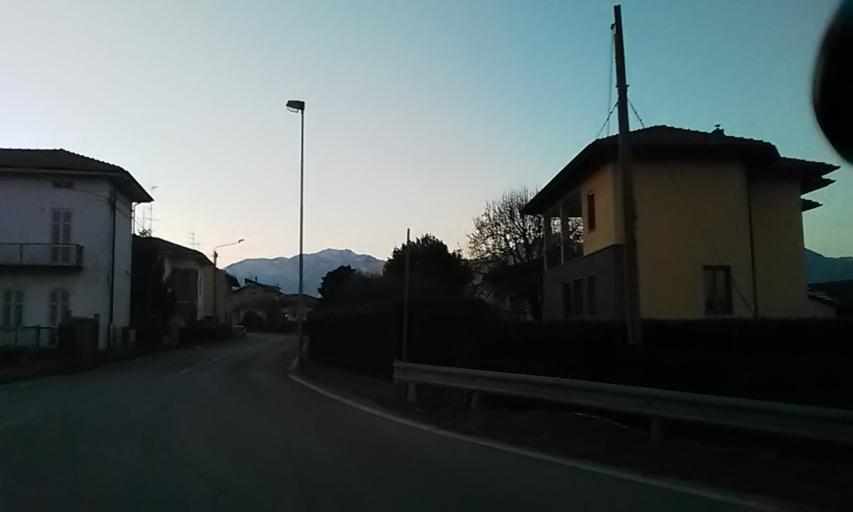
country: IT
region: Piedmont
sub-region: Provincia di Biella
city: Vigliano Biellese
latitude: 45.5572
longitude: 8.1028
